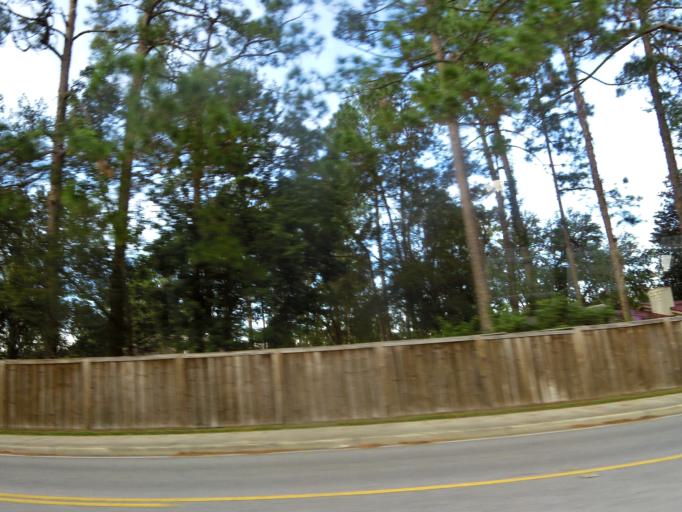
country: US
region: Florida
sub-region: Saint Johns County
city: Fruit Cove
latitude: 30.1590
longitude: -81.6159
